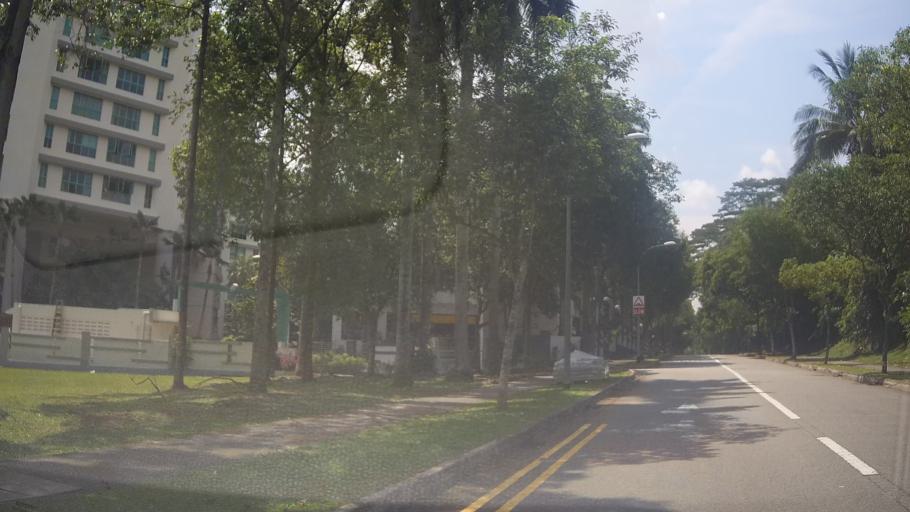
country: SG
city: Singapore
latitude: 1.3463
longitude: 103.7745
